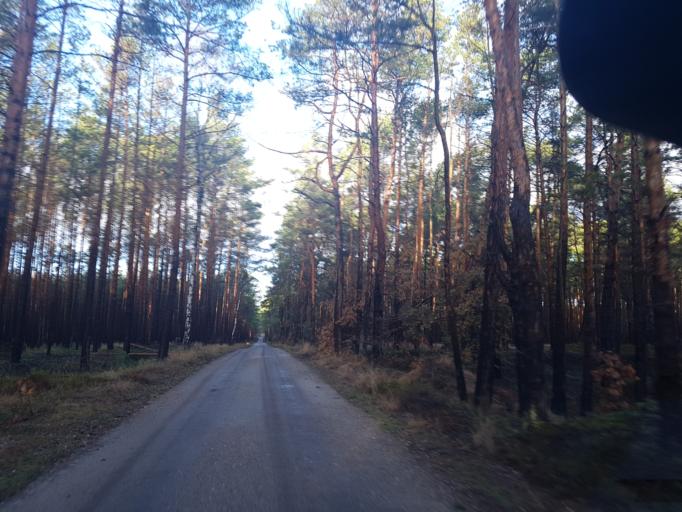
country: DE
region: Brandenburg
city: Ruckersdorf
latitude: 51.5853
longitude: 13.5986
